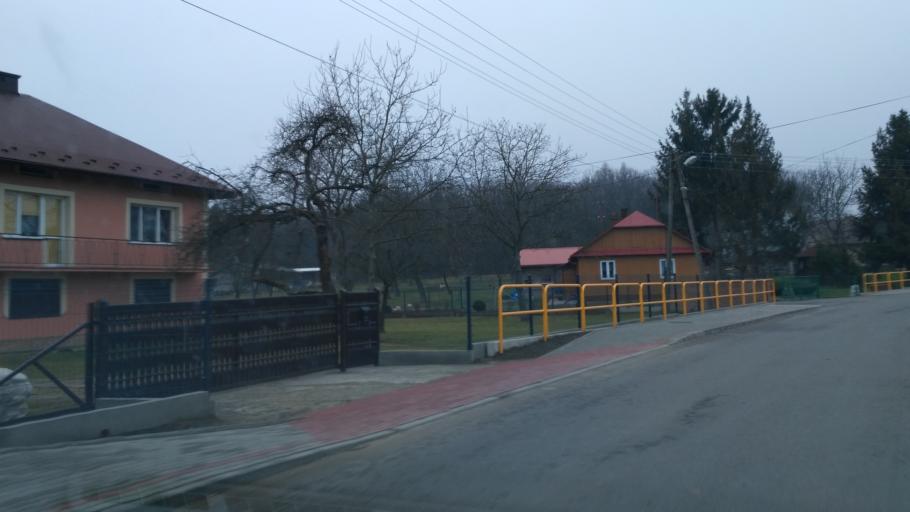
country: PL
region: Subcarpathian Voivodeship
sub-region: Powiat jaroslawski
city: Pawlosiow
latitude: 49.9827
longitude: 22.6335
